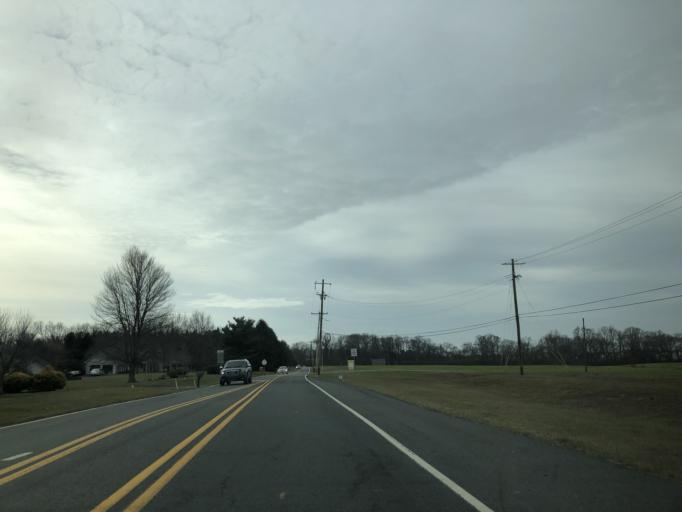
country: US
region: Delaware
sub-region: New Castle County
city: Middletown
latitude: 39.4982
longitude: -75.6871
